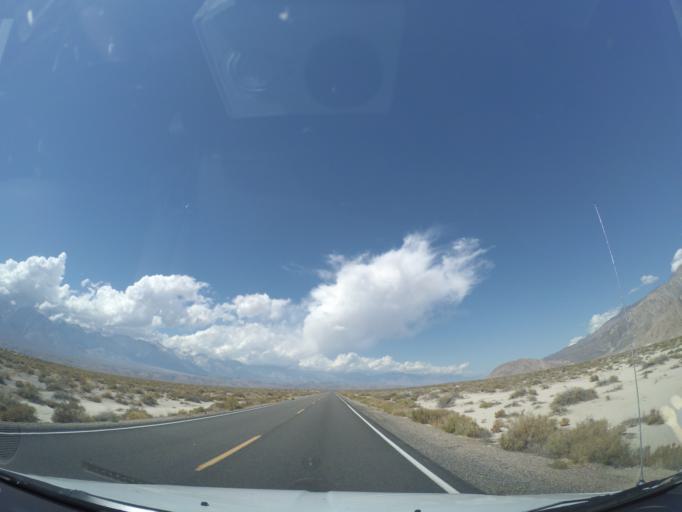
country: US
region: California
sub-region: Inyo County
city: Lone Pine
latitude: 36.5593
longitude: -117.9667
